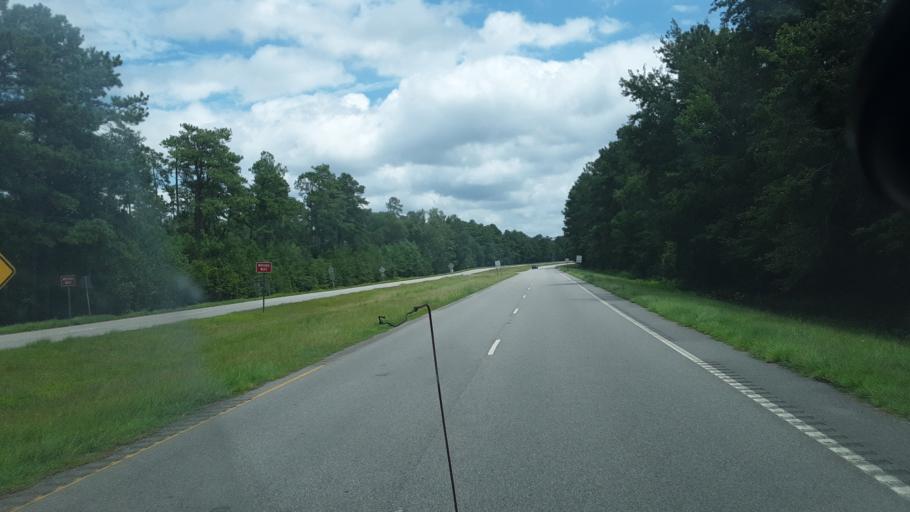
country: US
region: North Carolina
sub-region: Columbus County
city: Tabor City
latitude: 34.1186
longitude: -78.9760
